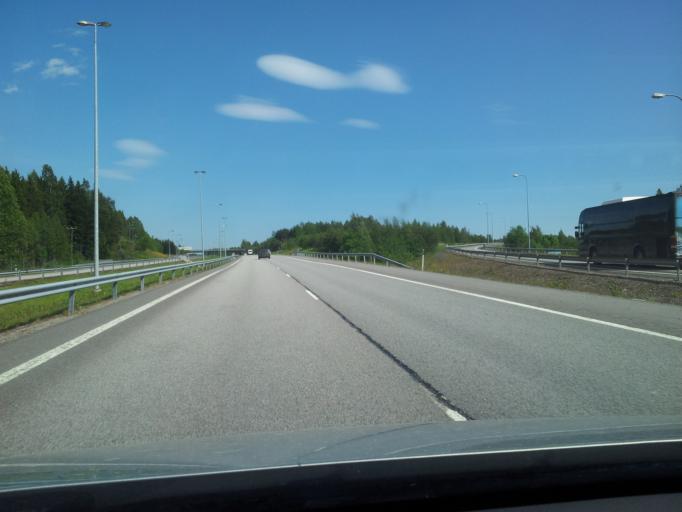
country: FI
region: Uusimaa
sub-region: Loviisa
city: Perna
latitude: 60.4918
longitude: 25.9485
